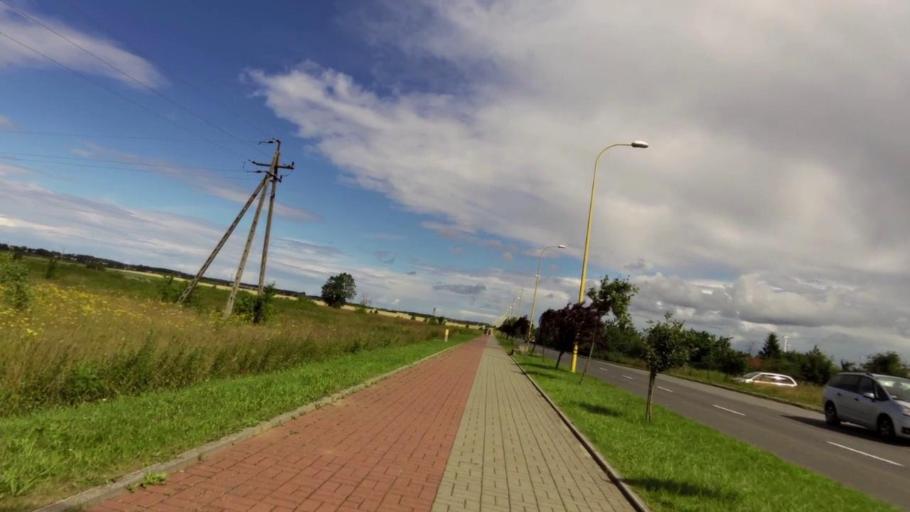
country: PL
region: West Pomeranian Voivodeship
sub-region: Powiat slawienski
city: Darlowo
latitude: 54.4297
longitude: 16.4138
